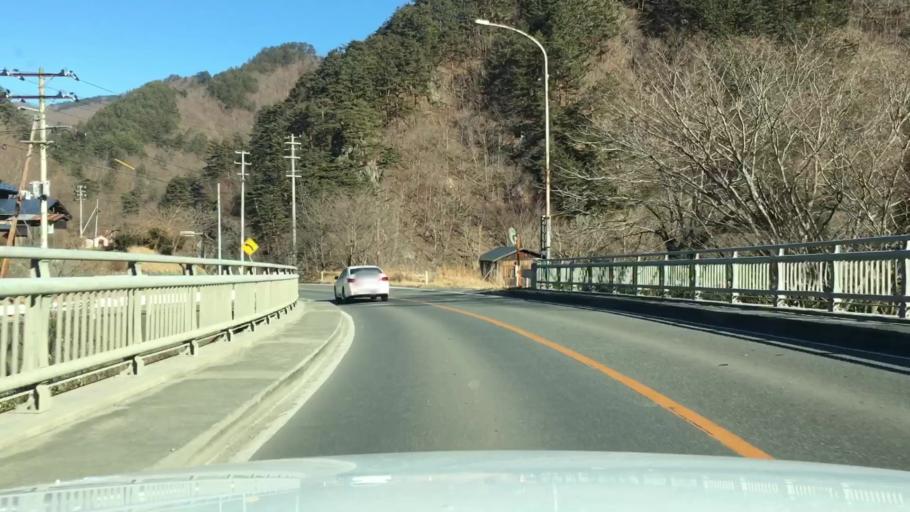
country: JP
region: Iwate
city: Miyako
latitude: 39.6037
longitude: 141.7731
